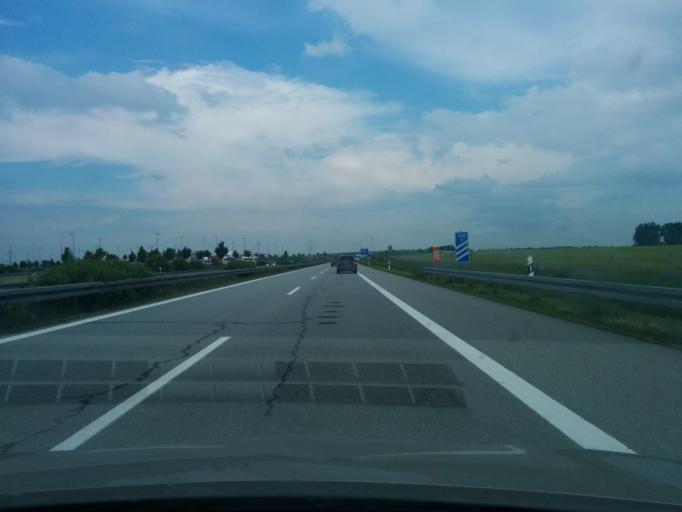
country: DE
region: Mecklenburg-Vorpommern
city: Jarmen
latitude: 53.8525
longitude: 13.3337
